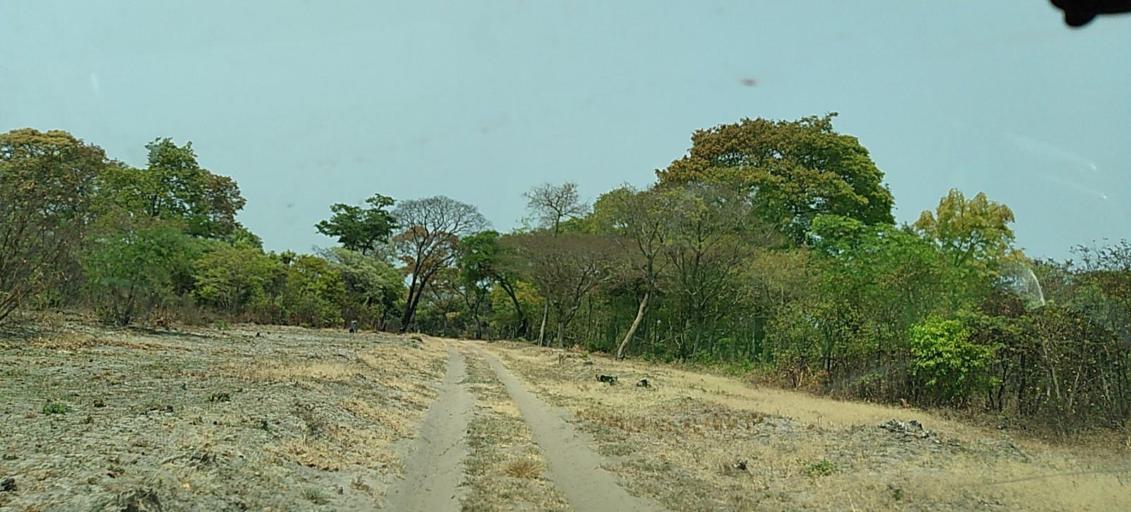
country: ZM
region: North-Western
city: Zambezi
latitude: -13.9276
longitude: 23.2255
